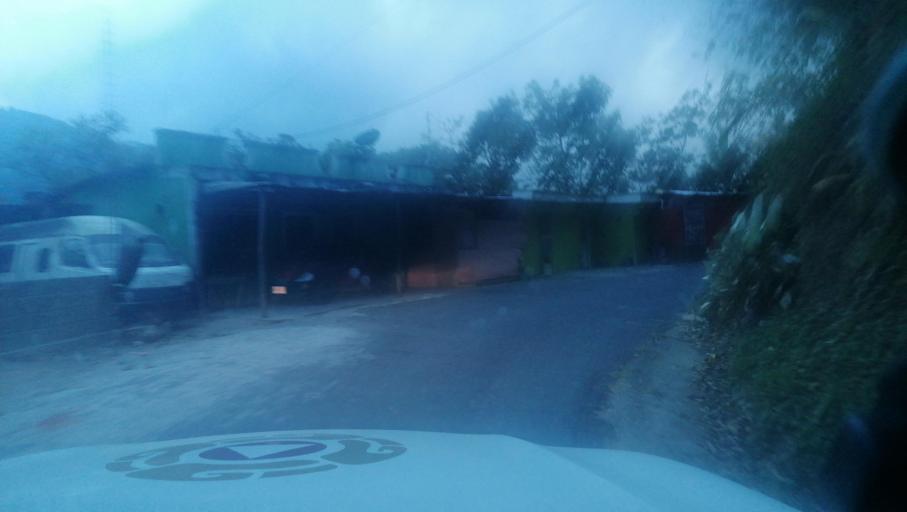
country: MX
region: Chiapas
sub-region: Cacahoatan
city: Benito Juarez
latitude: 15.1179
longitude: -92.2102
